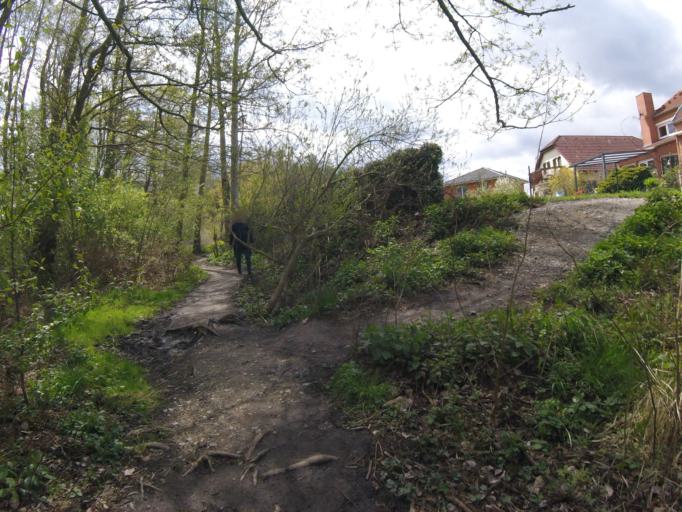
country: DE
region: Brandenburg
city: Bestensee
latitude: 52.2352
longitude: 13.6435
